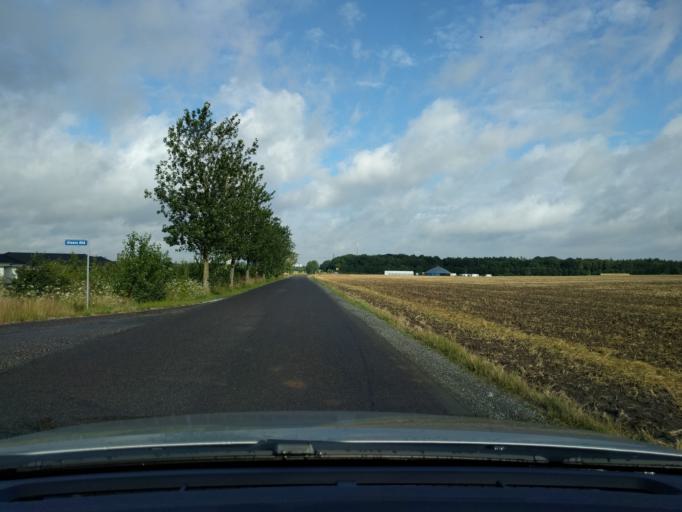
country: DK
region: South Denmark
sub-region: Odense Kommune
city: Bullerup
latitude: 55.4089
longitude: 10.4627
